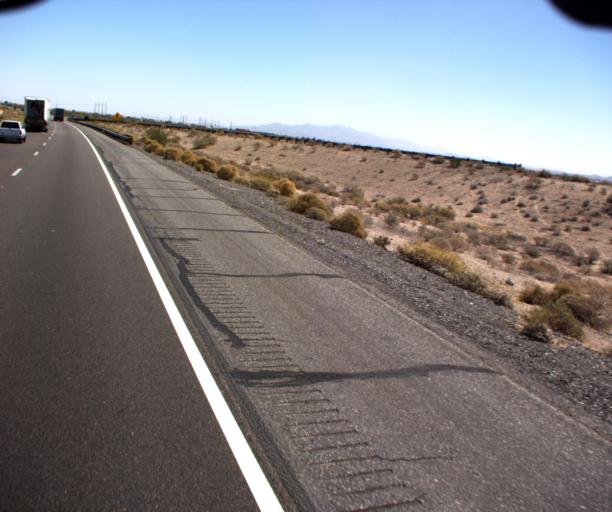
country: US
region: Arizona
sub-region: Maricopa County
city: Buckeye
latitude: 33.4270
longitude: -112.6215
